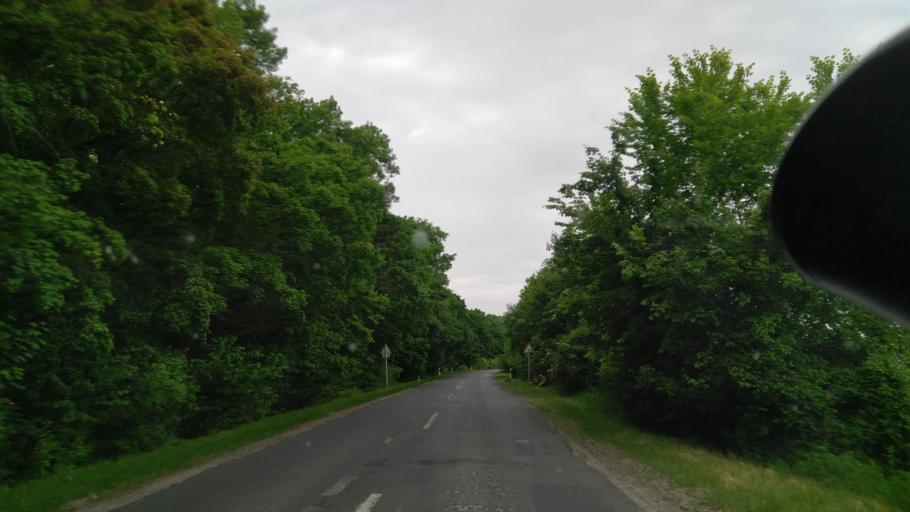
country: HU
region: Bekes
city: Doboz
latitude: 46.7306
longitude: 21.2690
